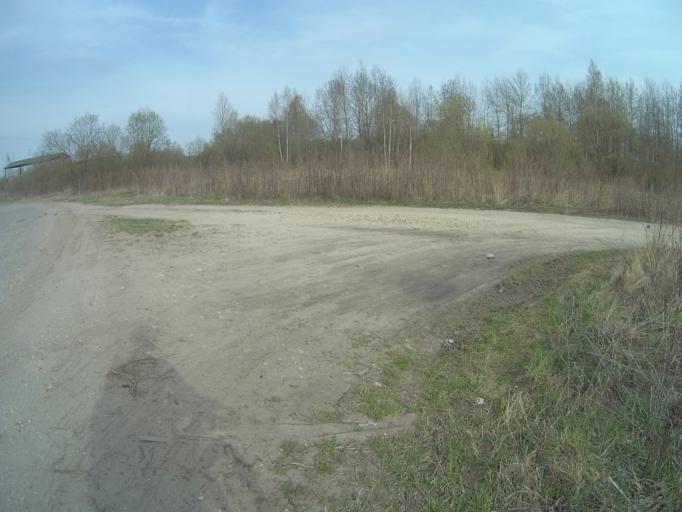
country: RU
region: Vladimir
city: Sudogda
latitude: 55.9731
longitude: 40.7256
